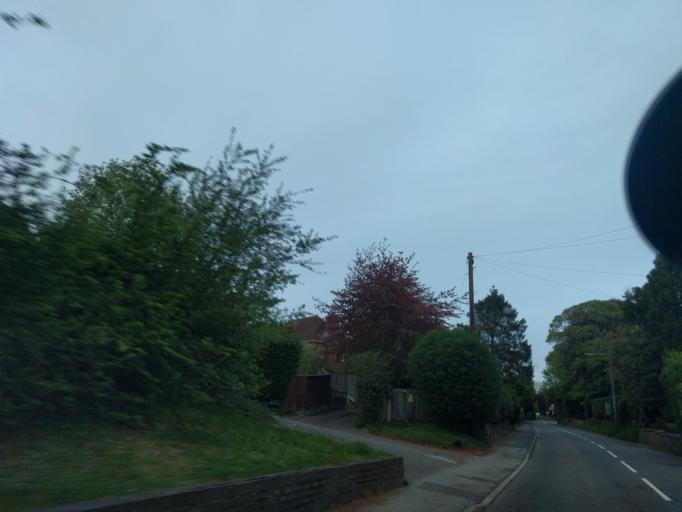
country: GB
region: England
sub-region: Wiltshire
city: Devizes
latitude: 51.3452
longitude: -1.9935
